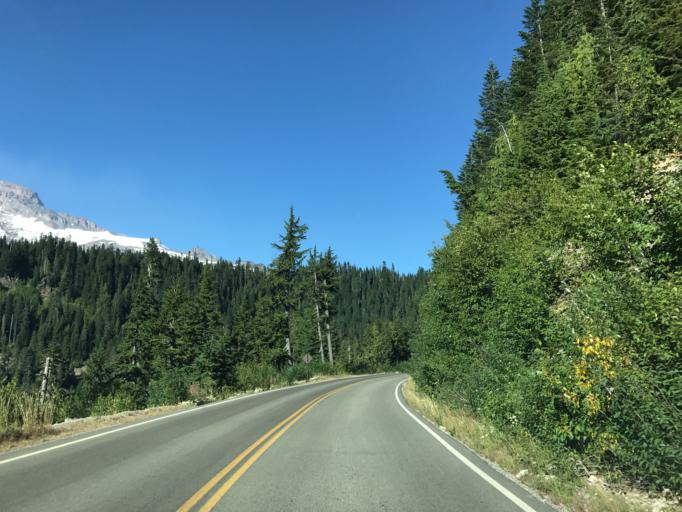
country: US
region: Washington
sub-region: Pierce County
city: Buckley
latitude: 46.7754
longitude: -121.7425
